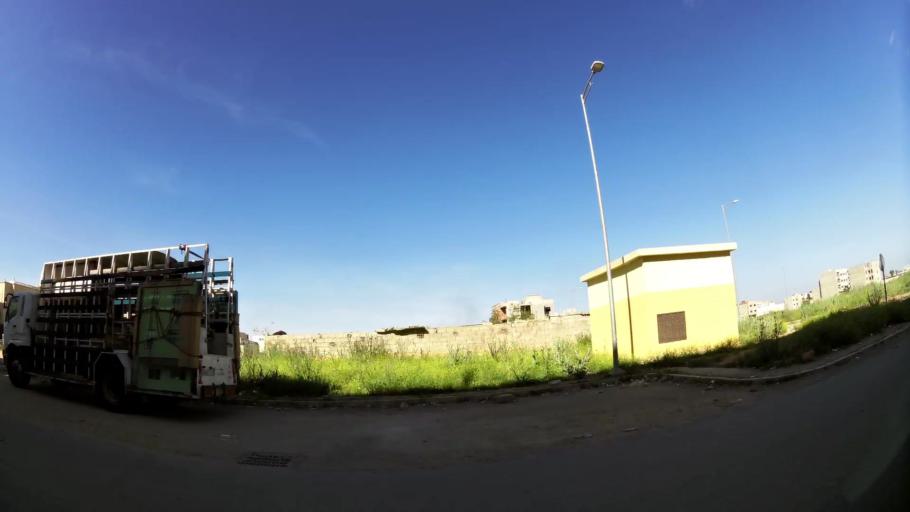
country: MA
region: Fes-Boulemane
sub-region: Fes
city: Fes
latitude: 34.0137
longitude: -4.9615
